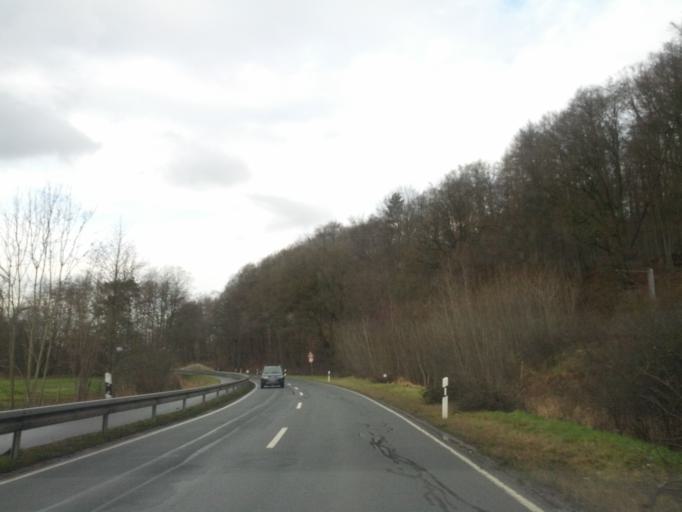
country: DE
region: Hesse
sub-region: Regierungsbezirk Kassel
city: Helsa
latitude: 51.2741
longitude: 9.6619
